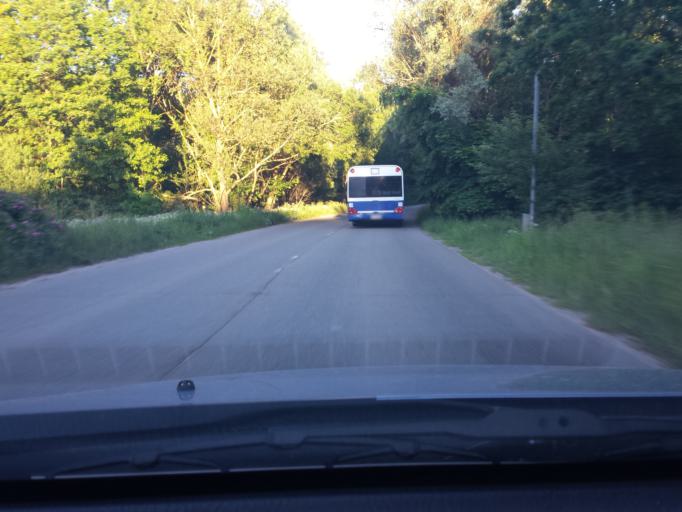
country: LV
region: Riga
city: Jaunciems
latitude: 57.0521
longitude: 24.1700
